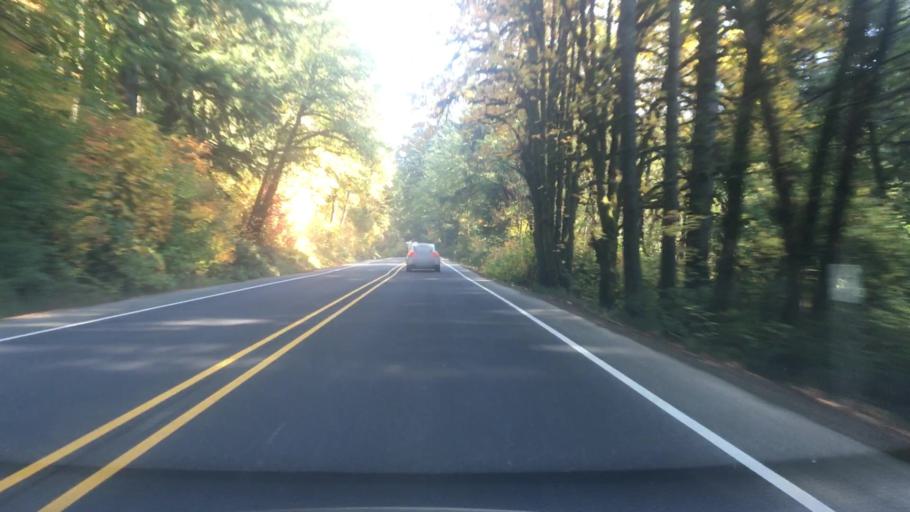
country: US
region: Oregon
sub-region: Lincoln County
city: Rose Lodge
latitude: 45.0555
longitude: -123.7612
